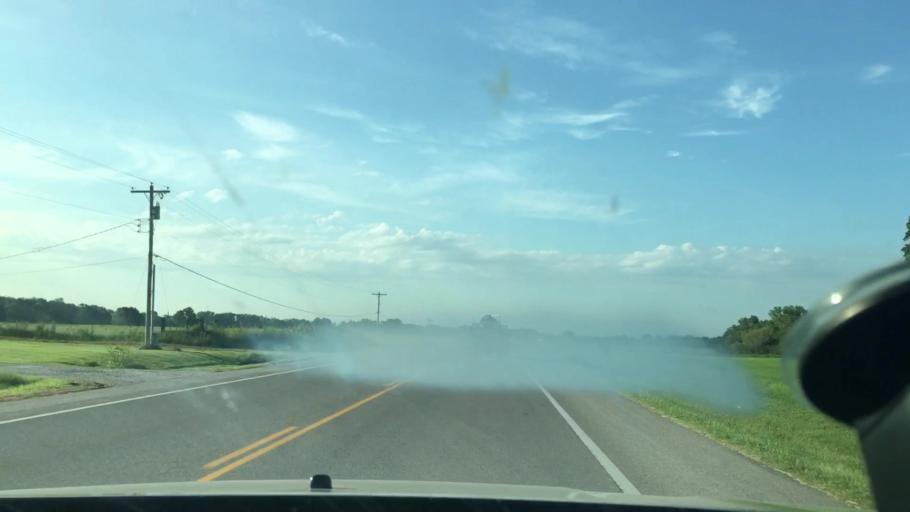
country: US
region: Oklahoma
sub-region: Garvin County
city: Wynnewood
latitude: 34.6624
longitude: -97.2038
